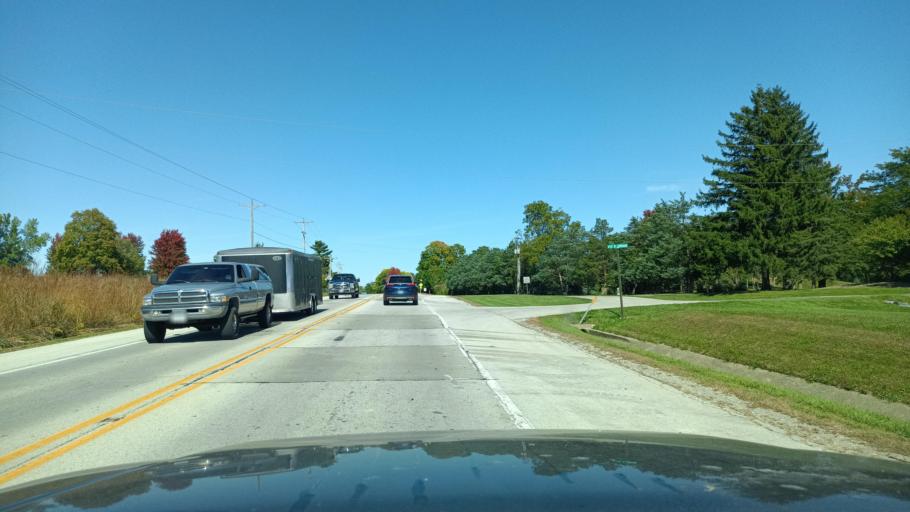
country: US
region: Illinois
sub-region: Champaign County
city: Mahomet
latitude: 40.2018
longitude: -88.3957
